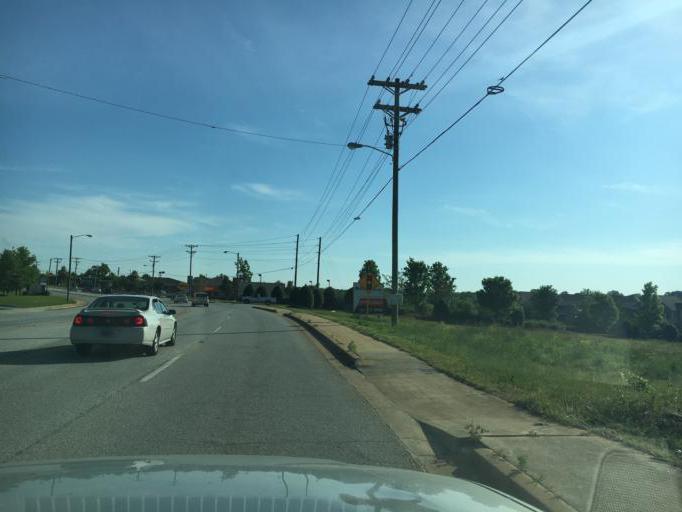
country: US
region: South Carolina
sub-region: Greenville County
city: Mauldin
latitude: 34.8033
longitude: -82.2849
